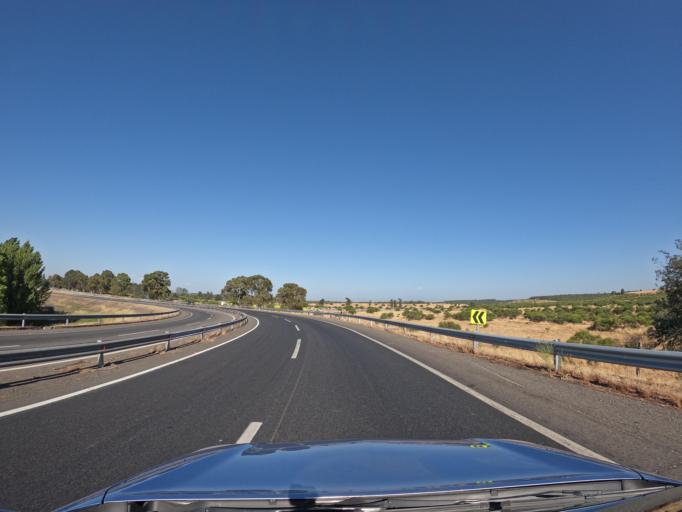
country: CL
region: Biobio
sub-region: Provincia de Nuble
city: Bulnes
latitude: -36.6560
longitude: -72.2290
